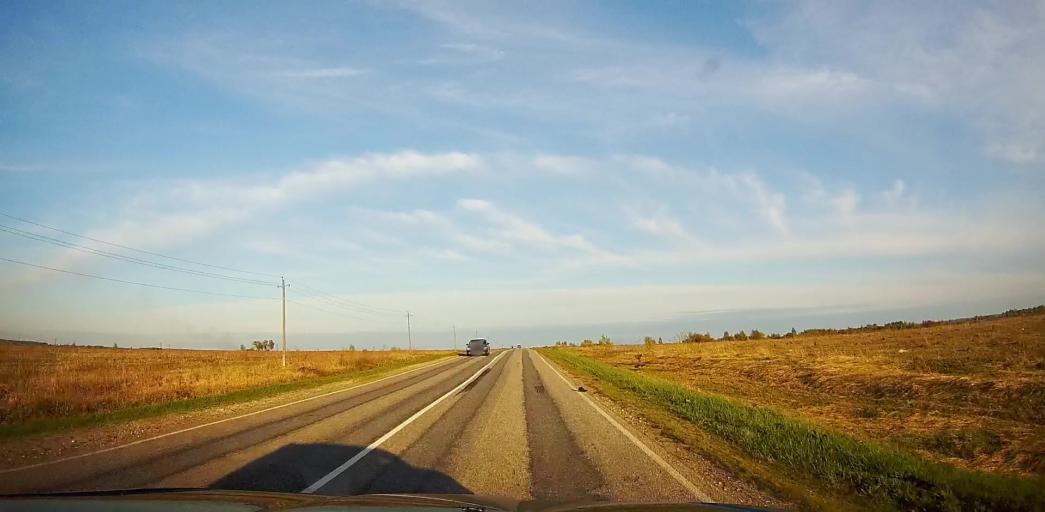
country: RU
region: Moskovskaya
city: Bronnitsy
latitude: 55.2737
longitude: 38.2307
